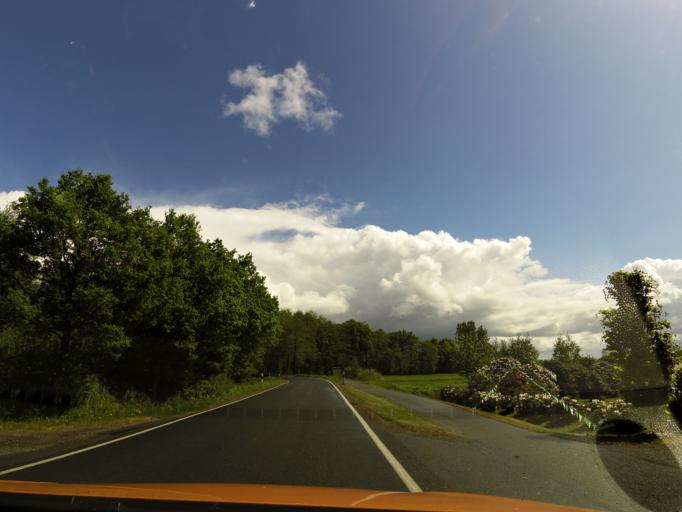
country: DE
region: Lower Saxony
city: Hude
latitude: 53.1500
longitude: 8.3721
